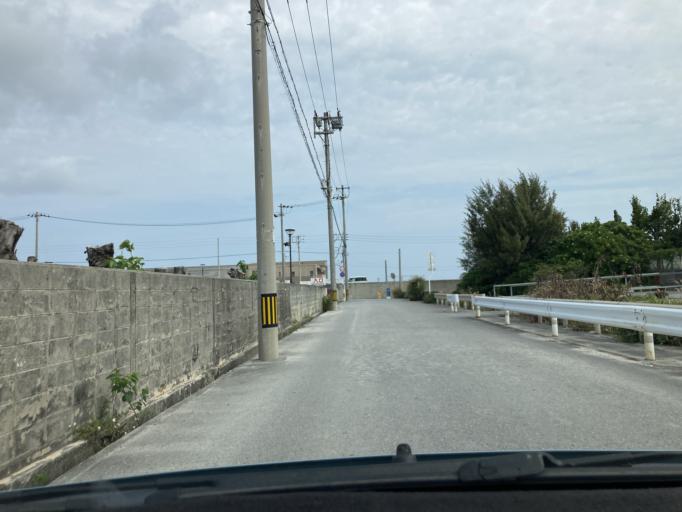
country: JP
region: Okinawa
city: Ginowan
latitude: 26.2727
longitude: 127.7152
